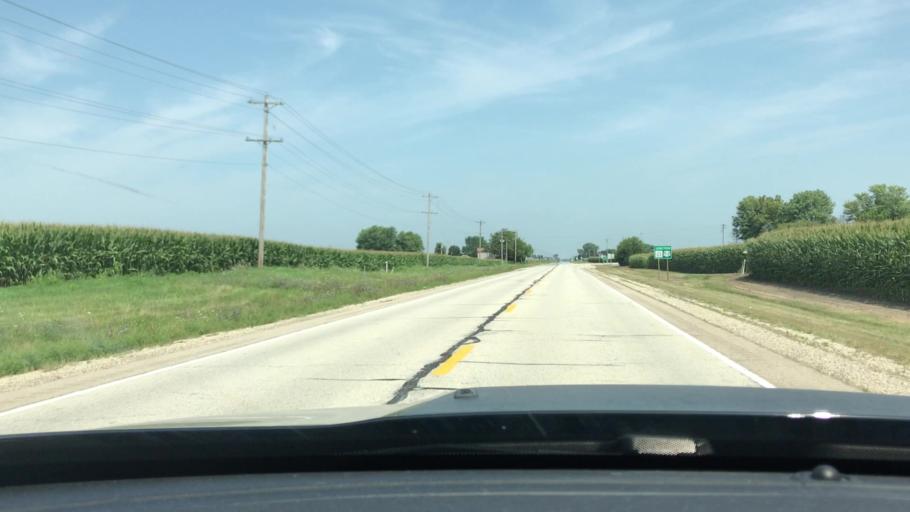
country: US
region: Illinois
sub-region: LaSalle County
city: Ottawa
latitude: 41.4826
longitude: -88.8151
